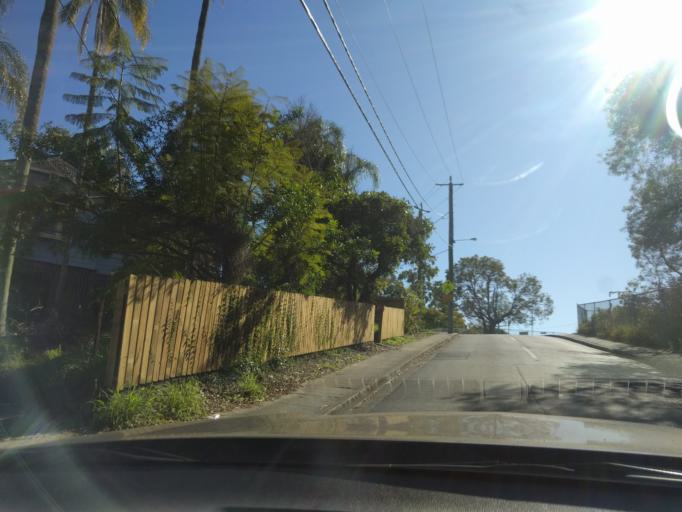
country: AU
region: Queensland
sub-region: Brisbane
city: Milton
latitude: -27.4764
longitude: 152.9966
